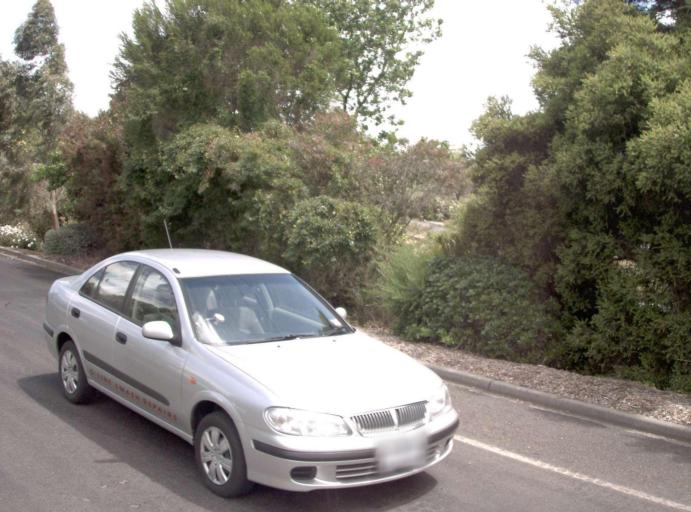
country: AU
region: Victoria
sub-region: Baw Baw
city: Warragul
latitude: -38.1510
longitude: 145.9354
